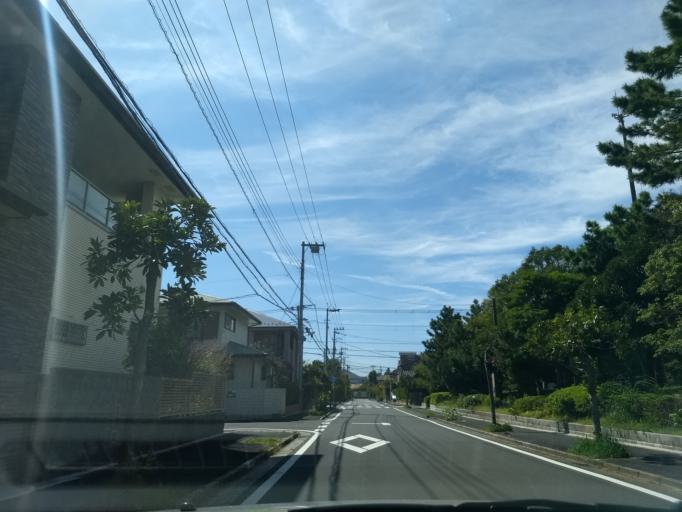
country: JP
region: Tokyo
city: Urayasu
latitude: 35.6404
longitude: 139.8983
